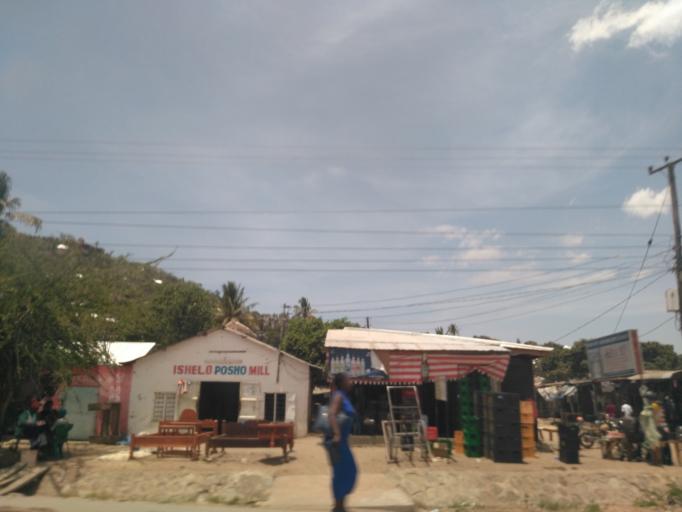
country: TZ
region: Mwanza
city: Mwanza
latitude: -2.5595
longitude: 32.9131
